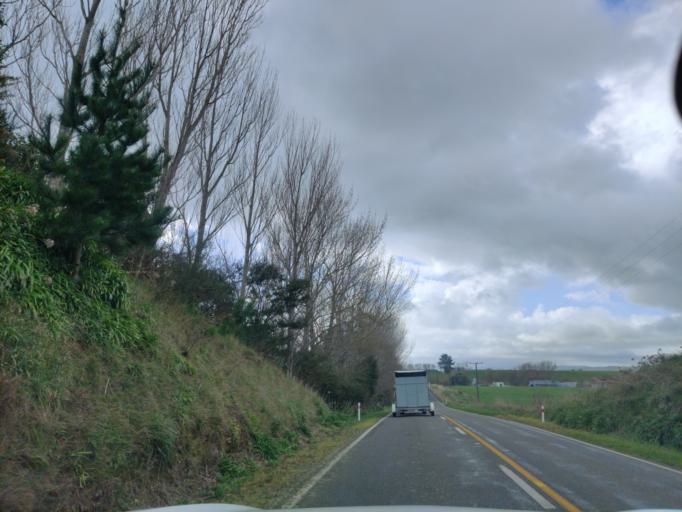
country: NZ
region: Manawatu-Wanganui
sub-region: Palmerston North City
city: Palmerston North
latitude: -40.4416
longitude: 175.5560
